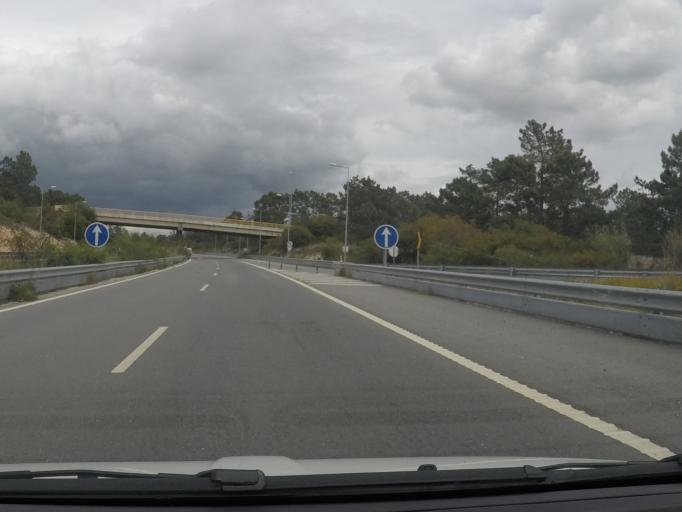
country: PT
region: Setubal
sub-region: Sines
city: Sines
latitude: 37.9737
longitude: -8.8096
